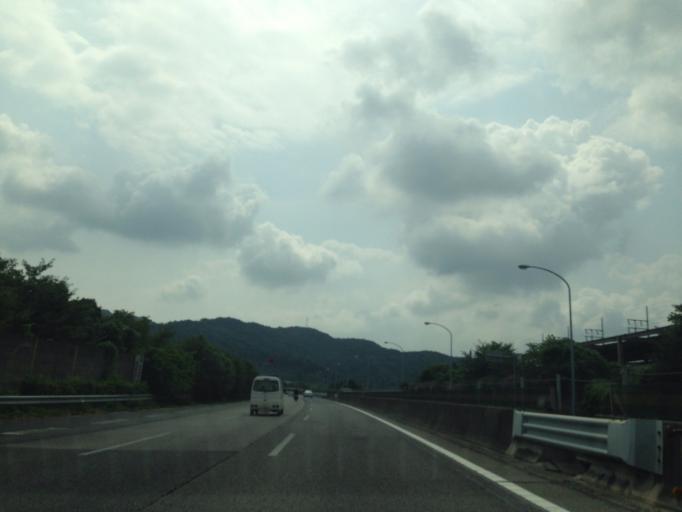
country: JP
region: Aichi
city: Gamagori
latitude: 34.8936
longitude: 137.2599
